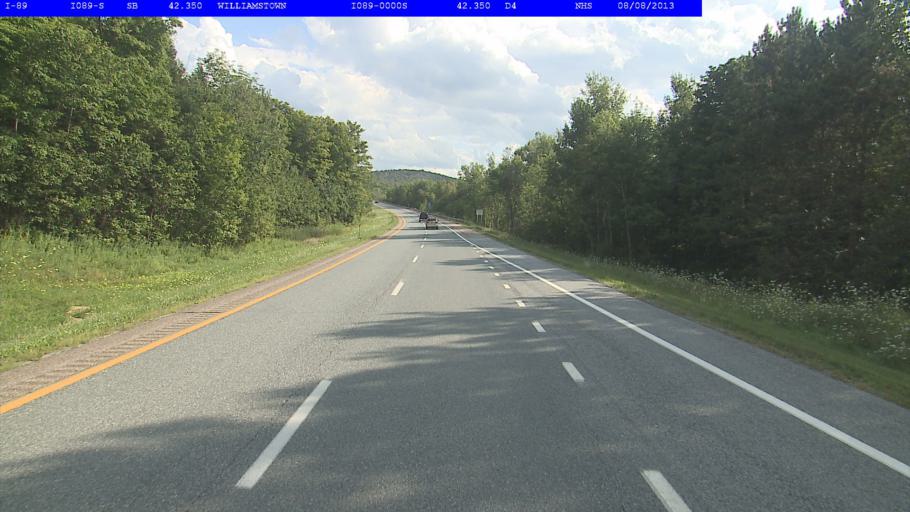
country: US
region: Vermont
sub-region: Washington County
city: Northfield
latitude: 44.1073
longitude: -72.6128
